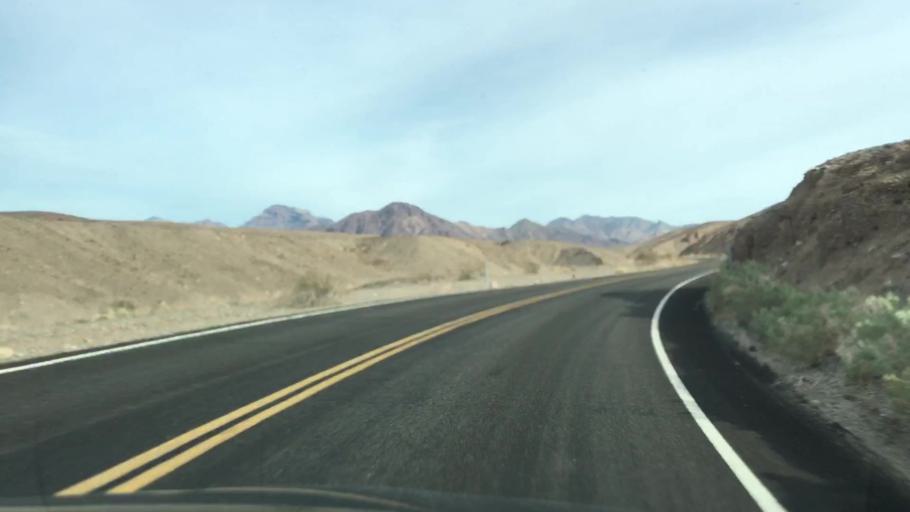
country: US
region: Nevada
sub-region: Nye County
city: Beatty
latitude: 36.6604
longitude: -117.0206
